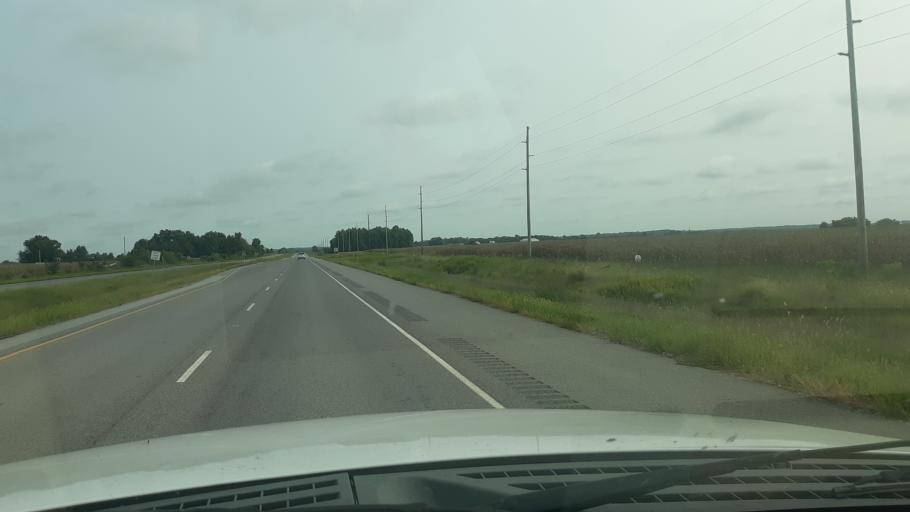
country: US
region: Illinois
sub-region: Saline County
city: Eldorado
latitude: 37.8470
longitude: -88.4116
